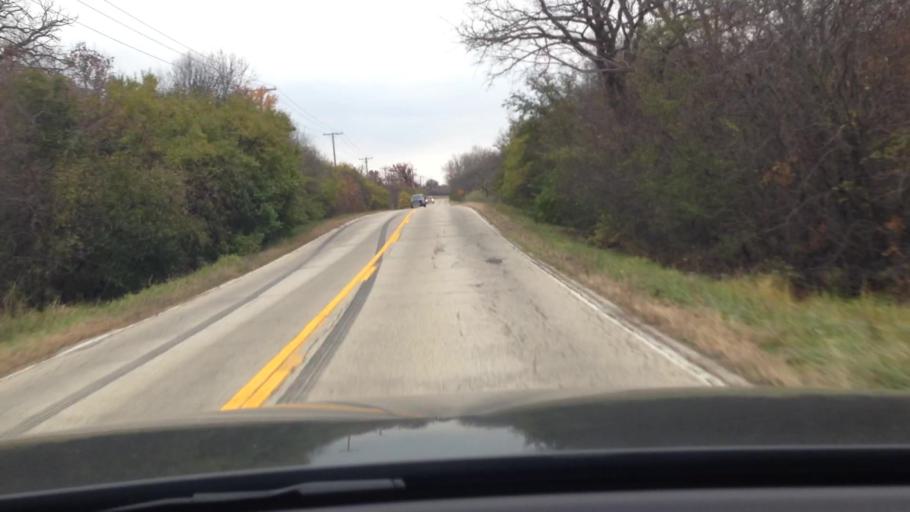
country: US
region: Illinois
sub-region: McHenry County
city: Woodstock
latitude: 42.2716
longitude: -88.4383
